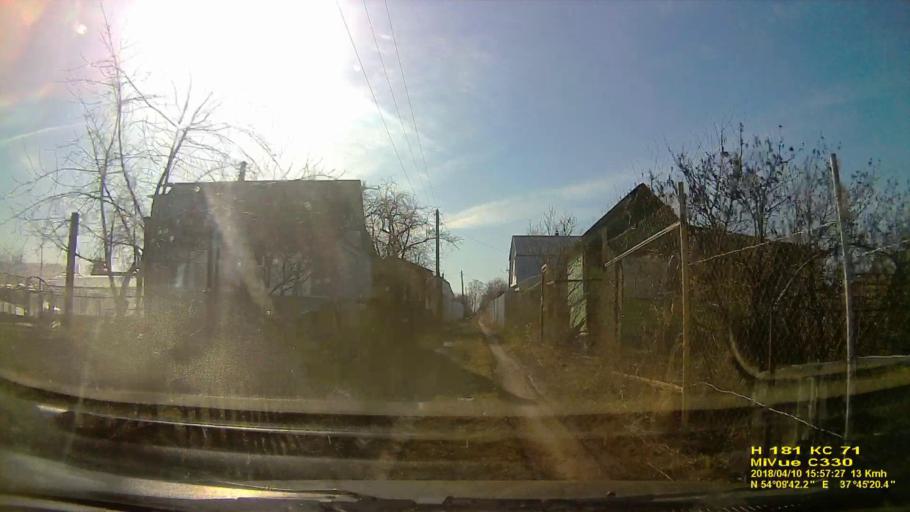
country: RU
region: Tula
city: Bolokhovo
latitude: 54.1617
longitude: 37.7556
